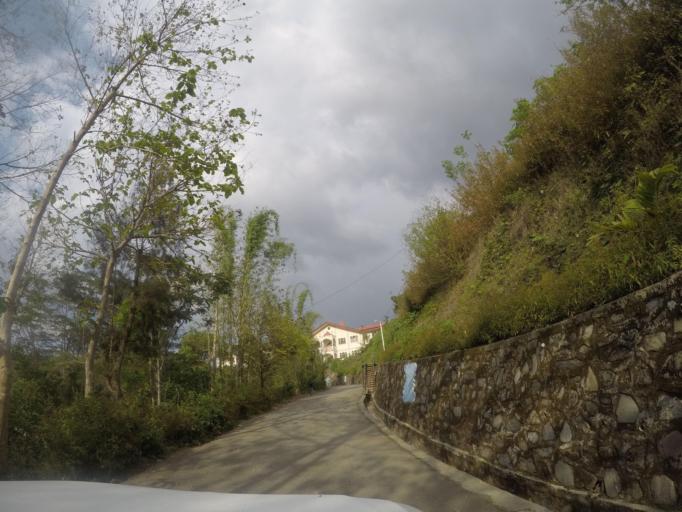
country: TL
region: Ermera
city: Gleno
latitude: -8.7212
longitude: 125.4377
